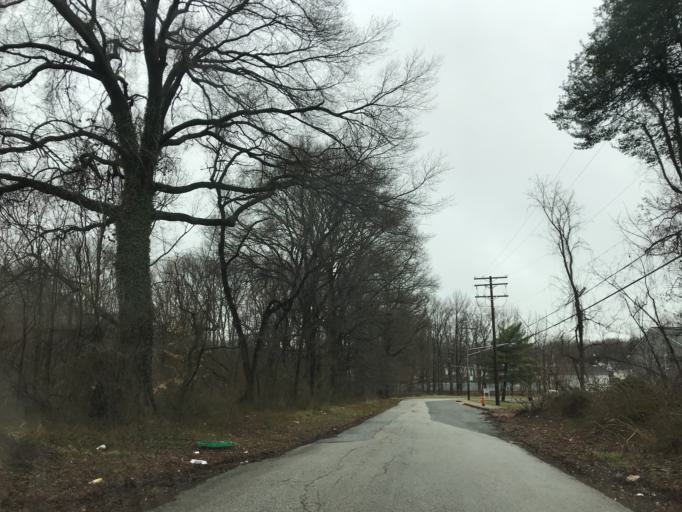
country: US
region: Maryland
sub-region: Baltimore County
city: Edgemere
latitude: 39.2358
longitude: -76.4360
